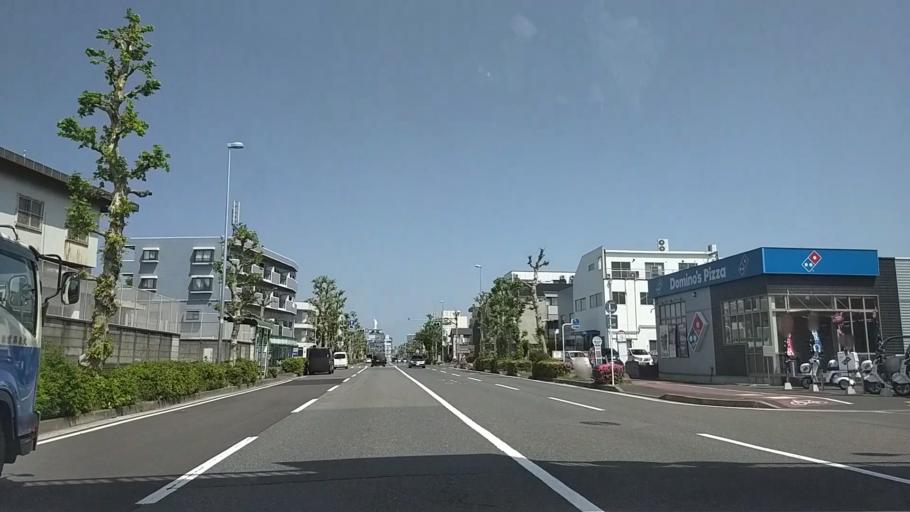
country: JP
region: Kanagawa
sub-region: Kawasaki-shi
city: Kawasaki
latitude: 35.5123
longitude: 139.6912
